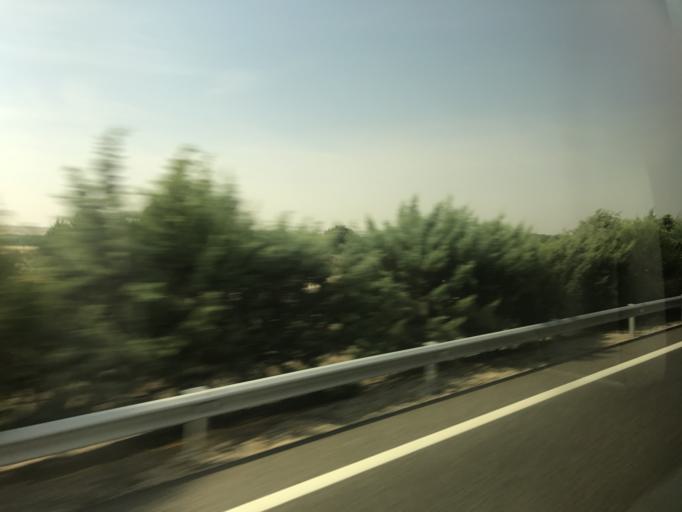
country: ES
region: Castille and Leon
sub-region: Provincia de Palencia
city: Palenzuela
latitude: 42.1105
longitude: -4.1703
